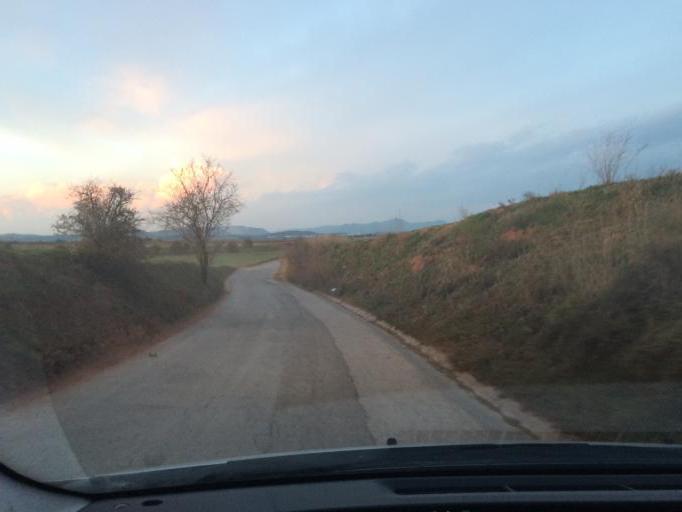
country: ES
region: Catalonia
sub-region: Provincia de Barcelona
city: Sant Fruitos de Bages
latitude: 41.7506
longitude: 1.8494
